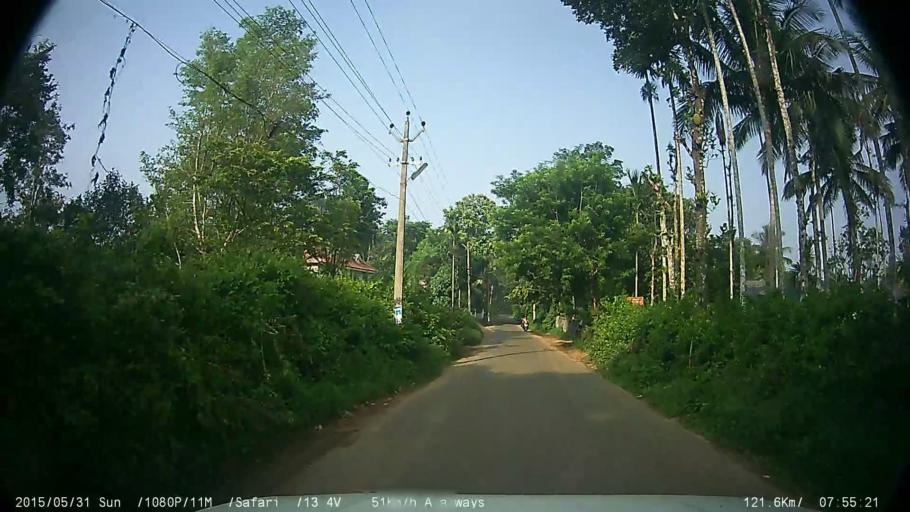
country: IN
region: Kerala
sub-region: Wayanad
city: Kalpetta
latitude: 11.6355
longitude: 76.0757
